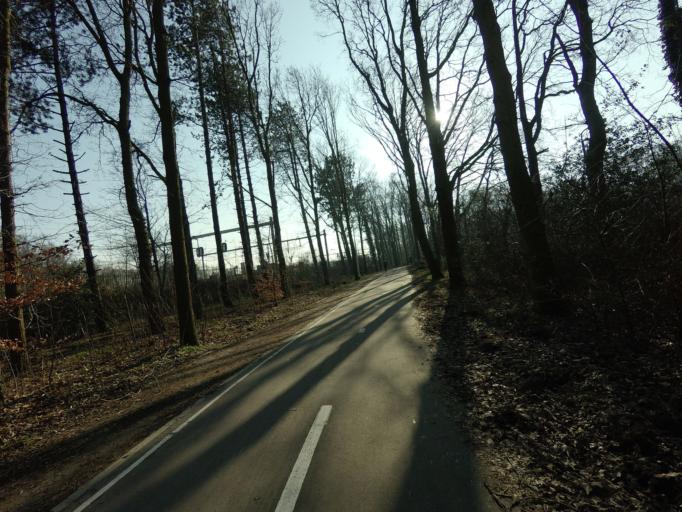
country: NL
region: North Holland
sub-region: Gemeente Velsen
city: Velsen-Zuid
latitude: 52.4347
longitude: 4.6324
